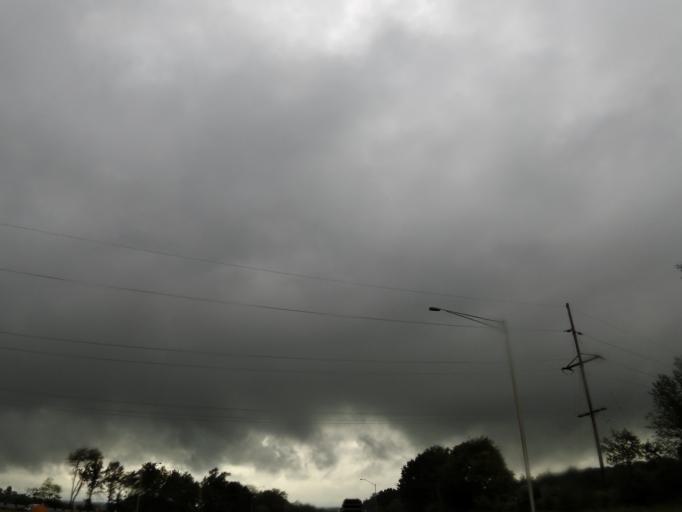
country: US
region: Illinois
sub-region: Jefferson County
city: Mount Vernon
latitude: 38.3386
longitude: -88.9600
